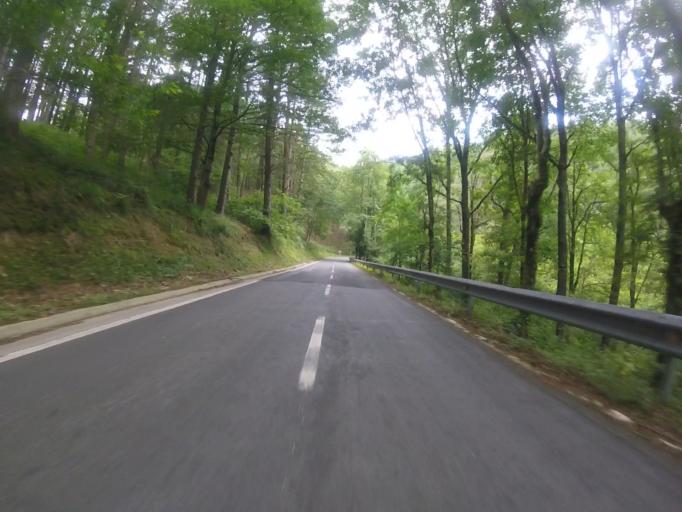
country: ES
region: Navarre
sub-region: Provincia de Navarra
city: Ezkurra
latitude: 43.0843
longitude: -1.8506
